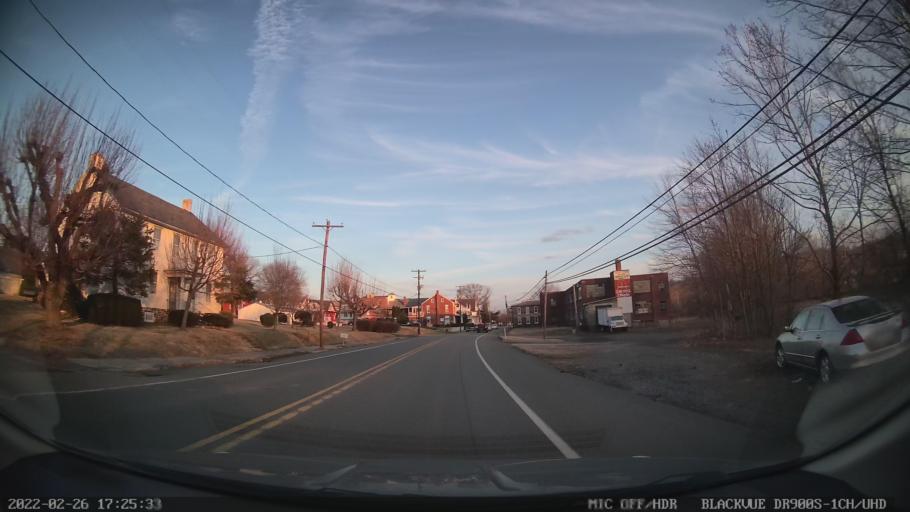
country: US
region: Pennsylvania
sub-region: Montgomery County
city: East Greenville
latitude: 40.4280
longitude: -75.5350
